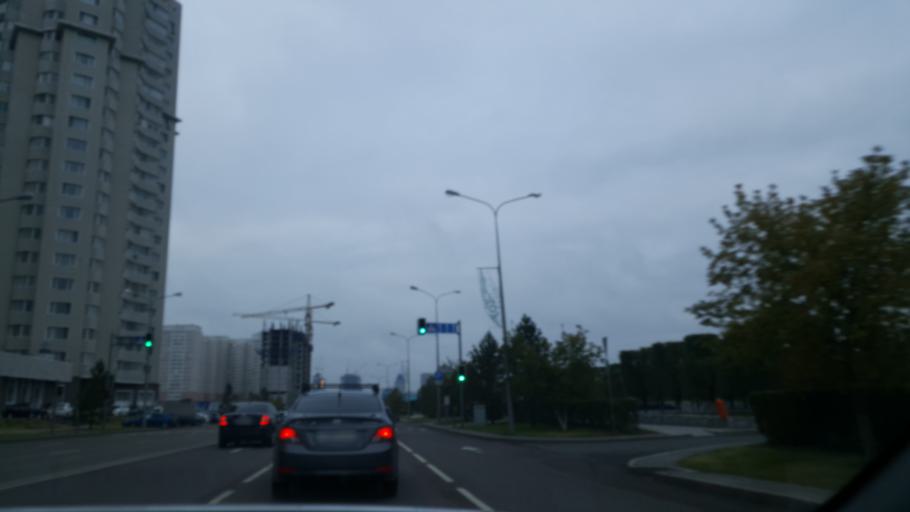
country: KZ
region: Astana Qalasy
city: Astana
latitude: 51.1202
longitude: 71.4651
